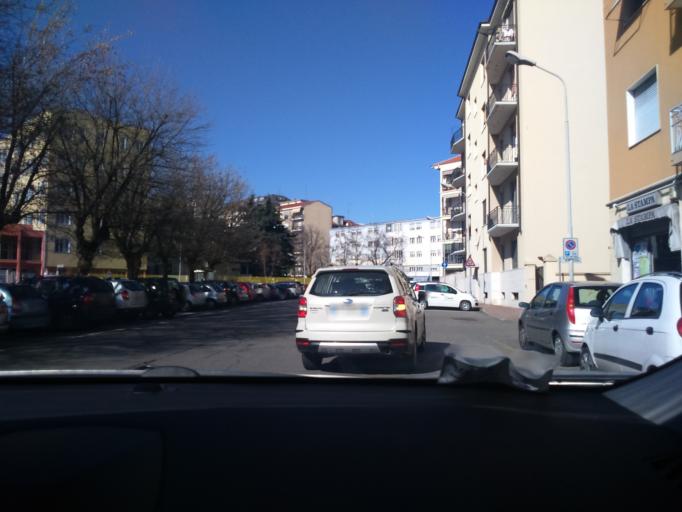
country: IT
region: Piedmont
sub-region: Provincia di Vercelli
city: Vercelli
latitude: 45.3177
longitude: 8.4172
